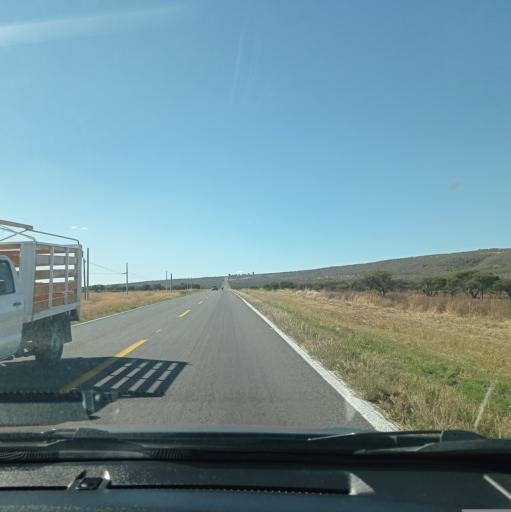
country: MX
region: Jalisco
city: San Miguel el Alto
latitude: 21.0169
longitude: -102.4885
